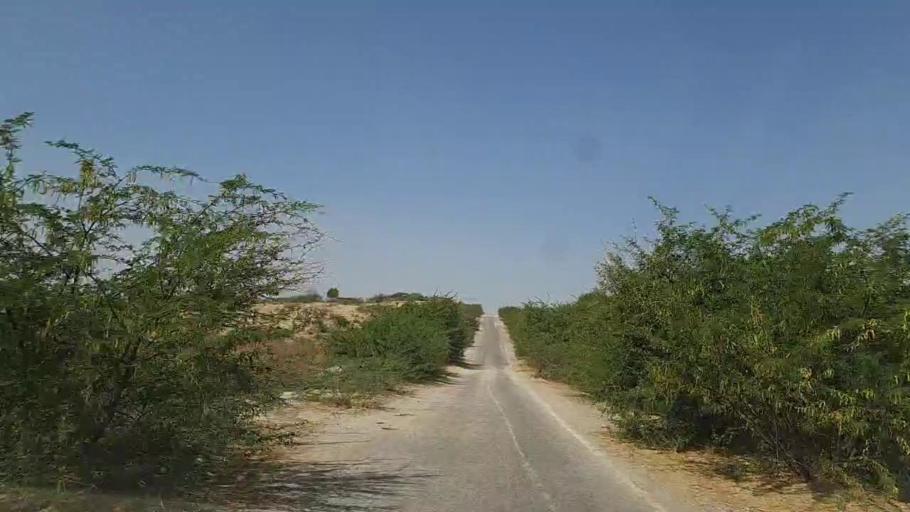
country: PK
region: Sindh
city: Naukot
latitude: 24.5869
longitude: 69.3176
